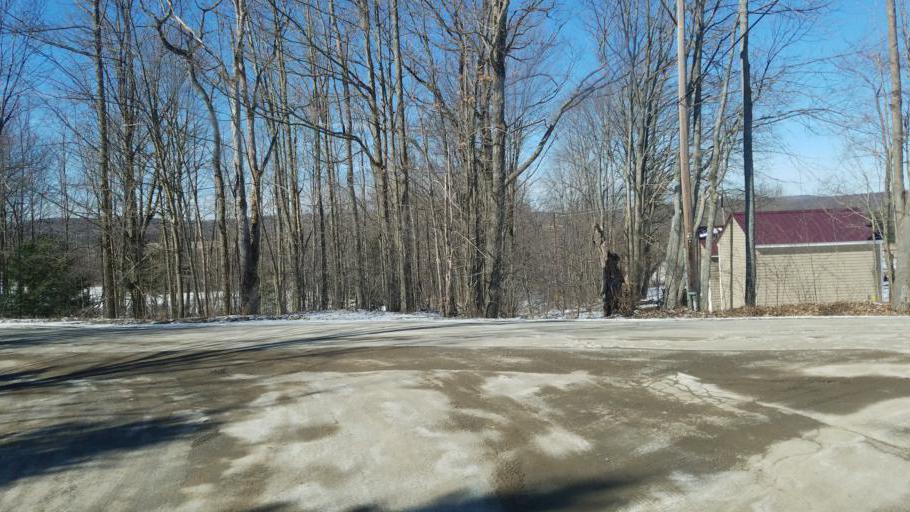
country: US
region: New York
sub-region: Allegany County
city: Wellsville
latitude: 42.0849
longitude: -78.0059
